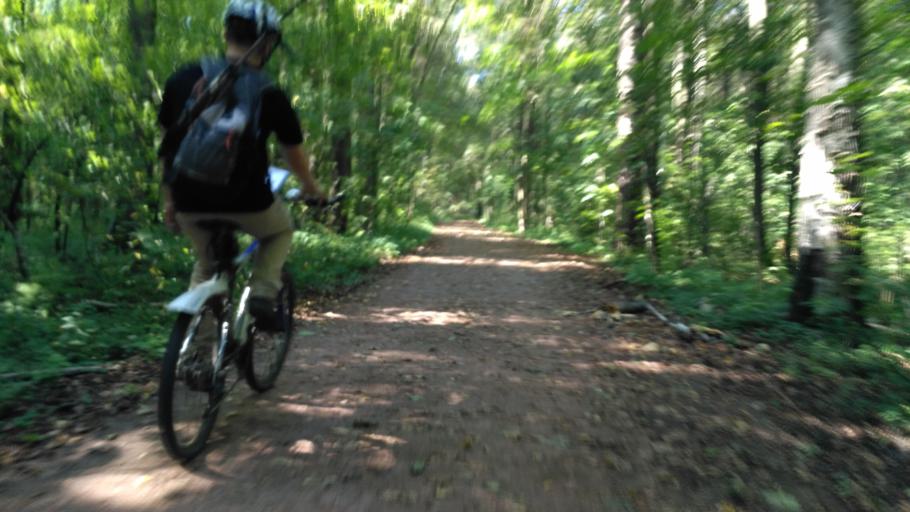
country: RU
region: Moskovskaya
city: Izmaylovo
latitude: 55.7830
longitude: 37.7735
